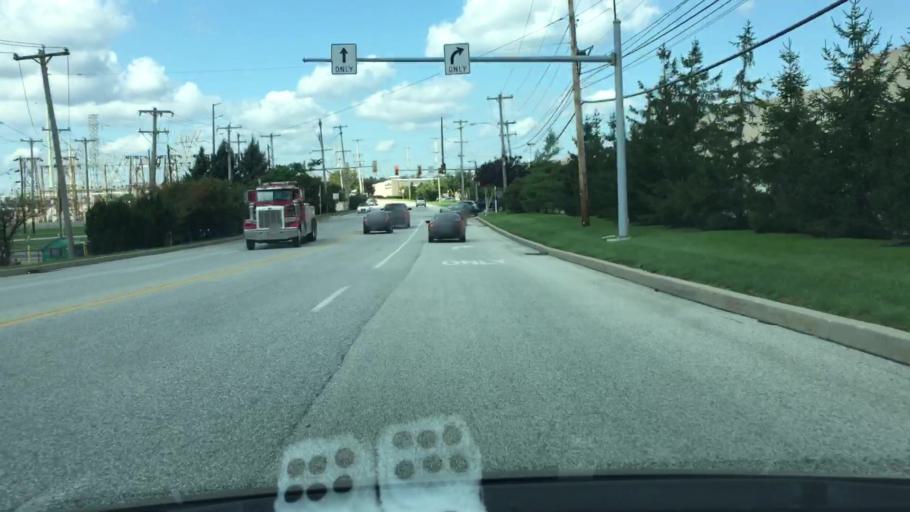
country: US
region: Pennsylvania
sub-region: Montgomery County
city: Plymouth Meeting
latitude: 40.1020
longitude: -75.2957
